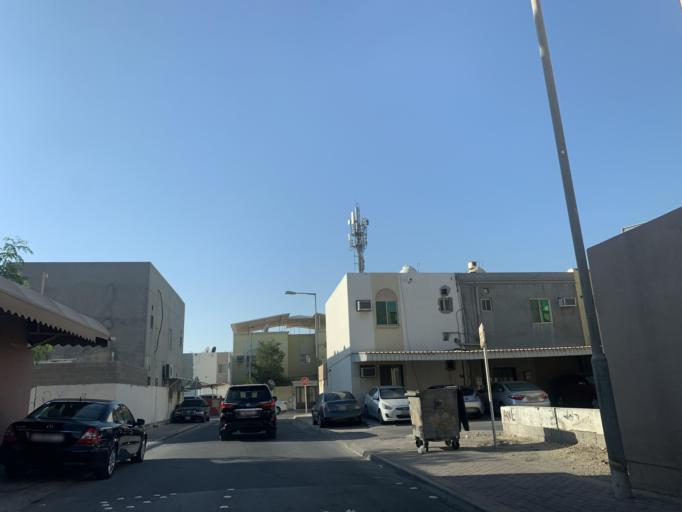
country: BH
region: Central Governorate
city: Madinat Hamad
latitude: 26.1124
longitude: 50.5087
